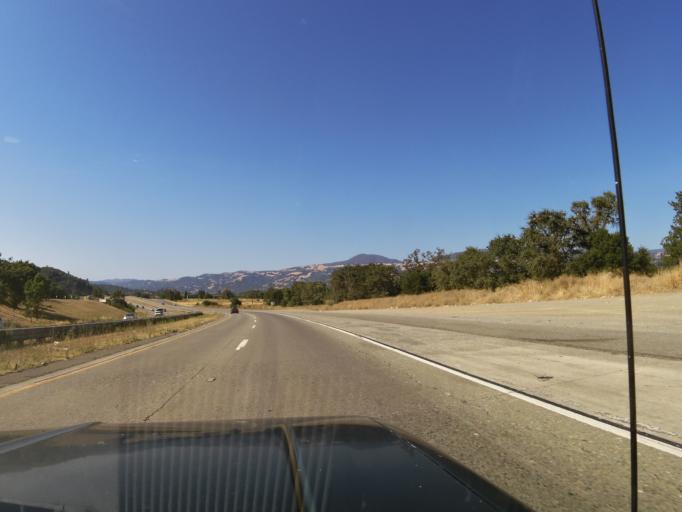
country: US
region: California
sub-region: Sonoma County
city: Healdsburg
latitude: 38.6519
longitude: -122.8714
